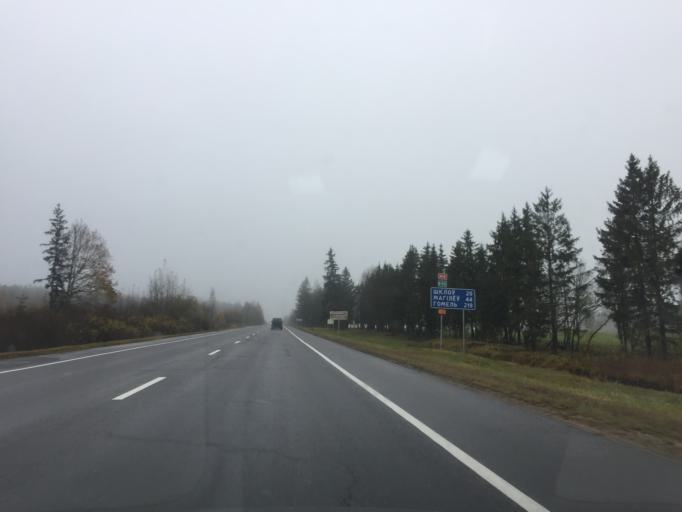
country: BY
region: Mogilev
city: Shklow
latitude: 54.2985
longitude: 30.4482
